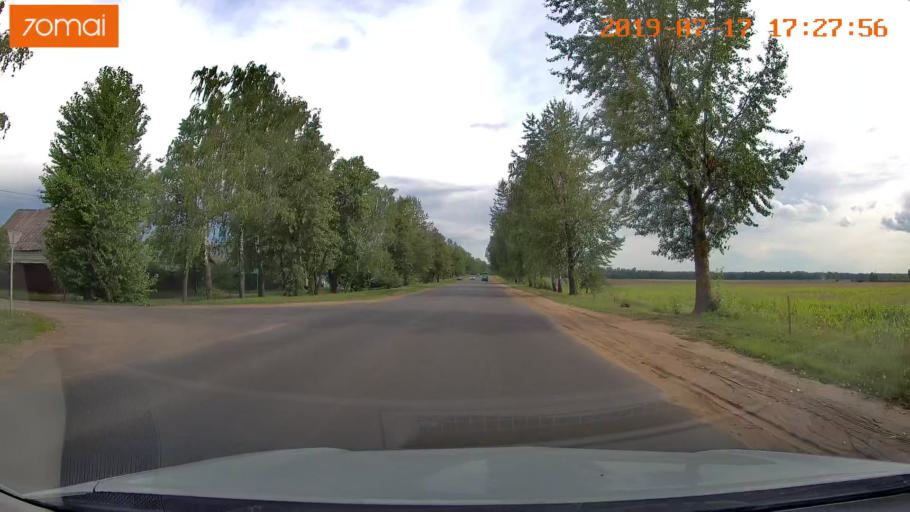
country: BY
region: Mogilev
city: Babruysk
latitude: 53.1339
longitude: 29.1664
